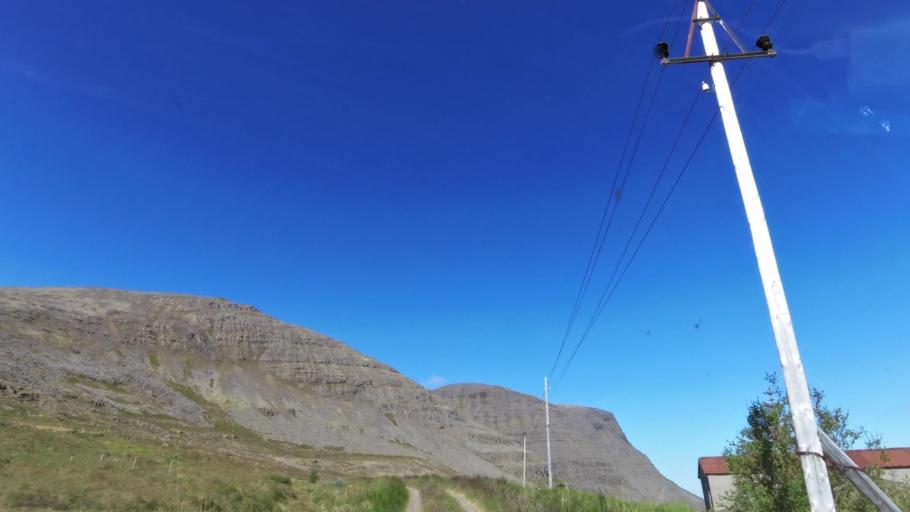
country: IS
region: West
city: Olafsvik
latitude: 65.6224
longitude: -23.8749
